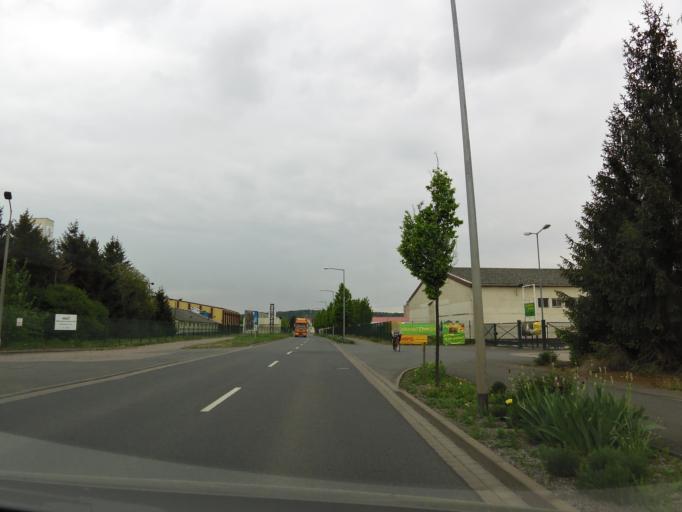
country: DE
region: Thuringia
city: Gotha
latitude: 50.9516
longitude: 10.7273
